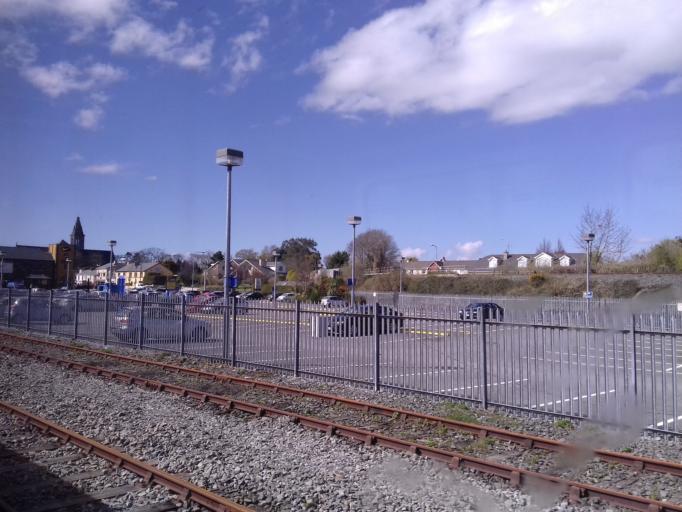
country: IE
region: Munster
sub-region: Ciarrai
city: Cill Airne
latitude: 52.0591
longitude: -9.4996
